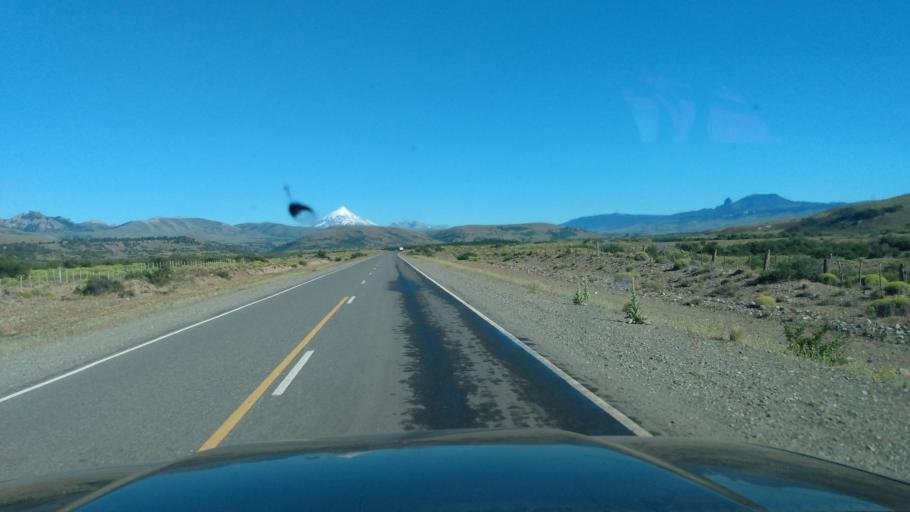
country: AR
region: Neuquen
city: Junin de los Andes
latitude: -39.8829
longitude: -71.1611
